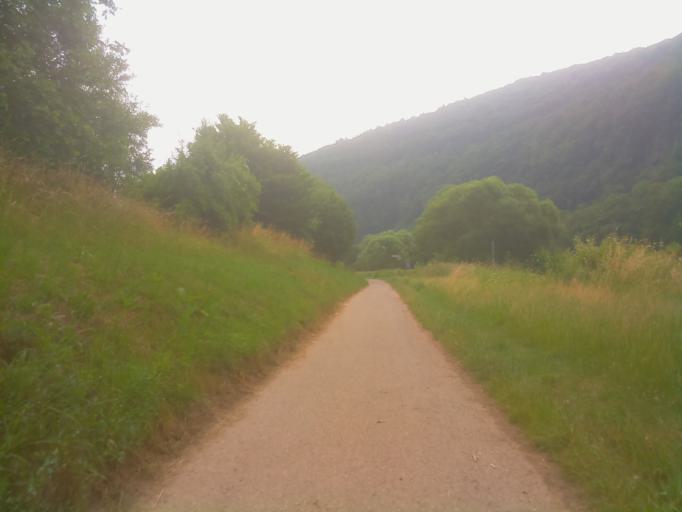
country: DE
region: Baden-Wuerttemberg
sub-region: Karlsruhe Region
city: Neckargemund
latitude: 49.3935
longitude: 8.8069
